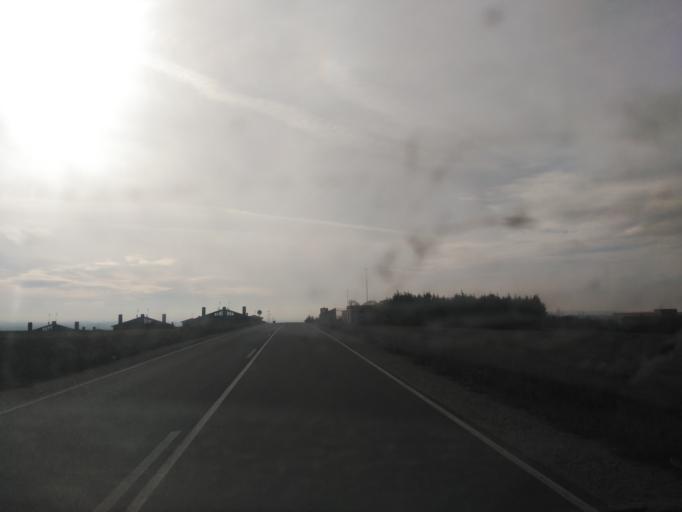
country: ES
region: Castille and Leon
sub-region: Provincia de Salamanca
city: Cabrerizos
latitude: 40.9842
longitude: -5.6042
